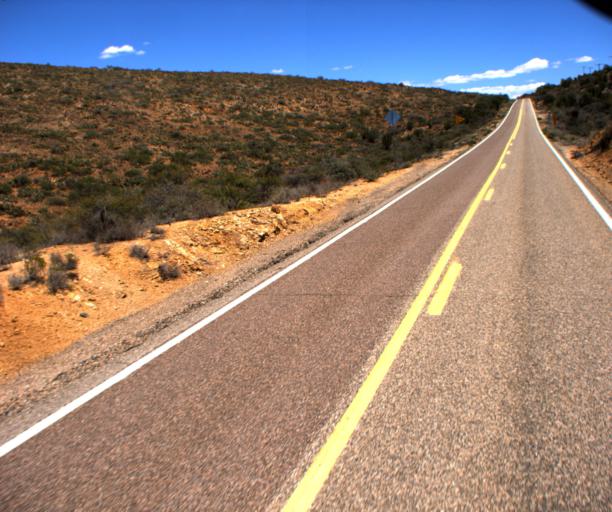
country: US
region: Arizona
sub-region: Yavapai County
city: Bagdad
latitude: 34.4435
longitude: -112.9508
